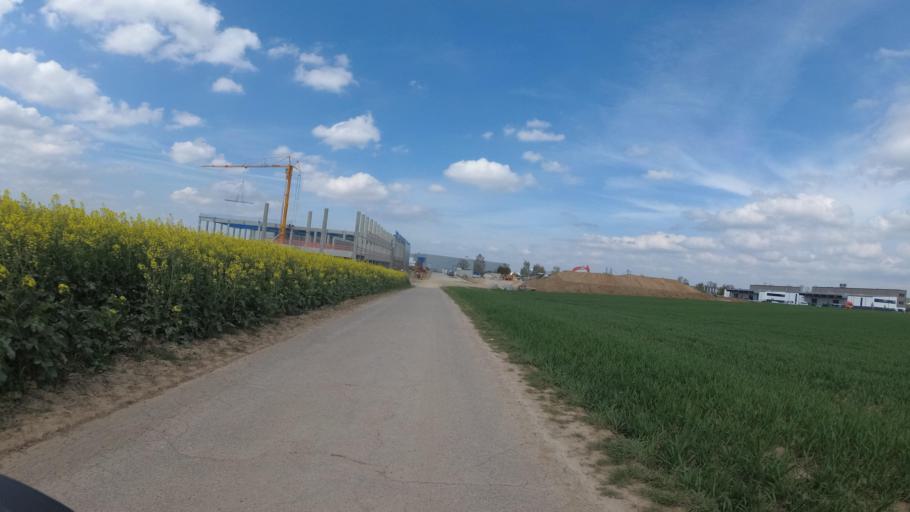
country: DE
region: Baden-Wuerttemberg
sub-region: Regierungsbezirk Stuttgart
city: Neuenstadt am Kocher
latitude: 49.2310
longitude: 9.3624
